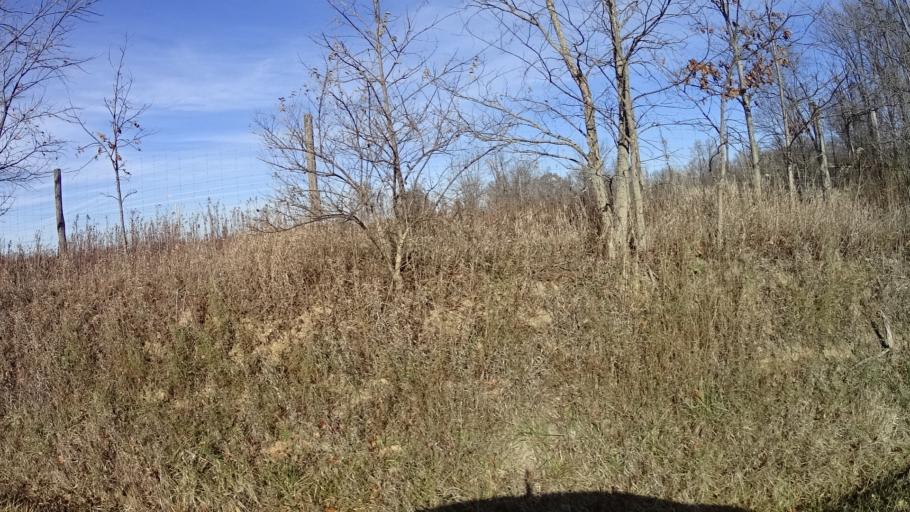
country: US
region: Ohio
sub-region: Lorain County
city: Wellington
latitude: 41.0858
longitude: -82.2720
